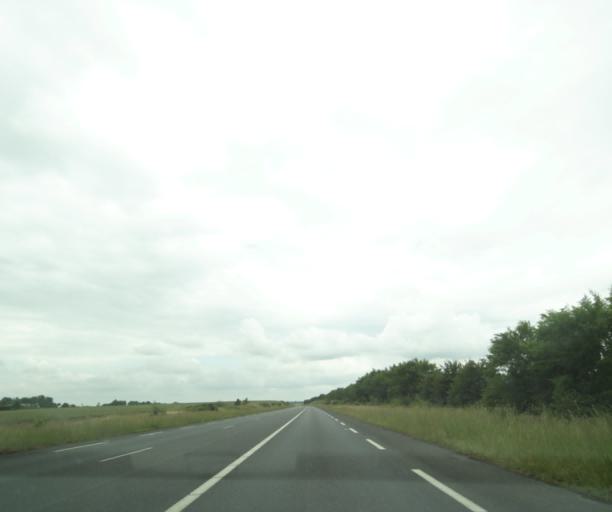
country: FR
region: Poitou-Charentes
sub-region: Departement des Deux-Sevres
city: Saint-Varent
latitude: 46.8828
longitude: -0.1950
